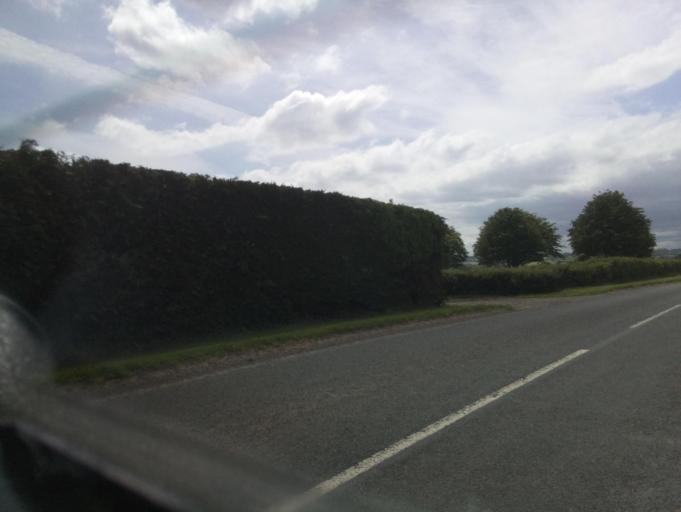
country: GB
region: England
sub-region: Herefordshire
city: Pencoyd
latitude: 51.9054
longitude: -2.7040
